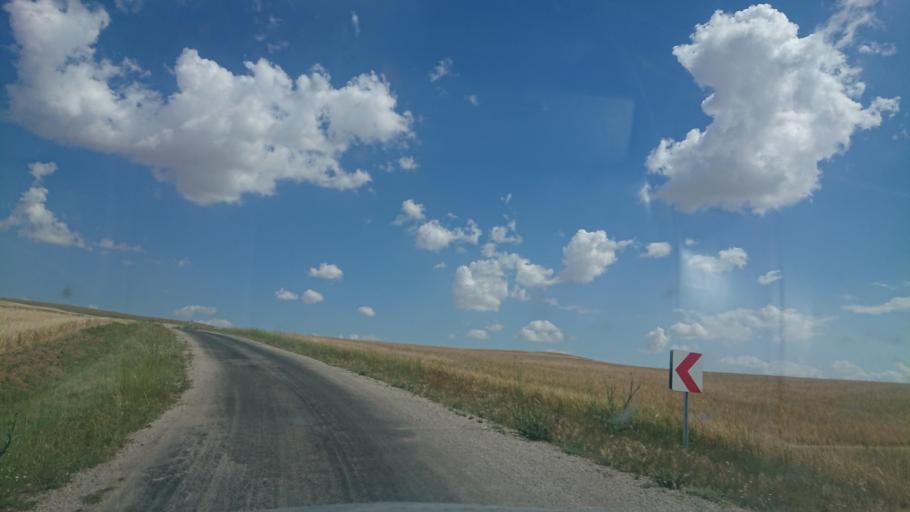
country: TR
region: Aksaray
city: Agacoren
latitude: 38.8078
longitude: 33.7999
